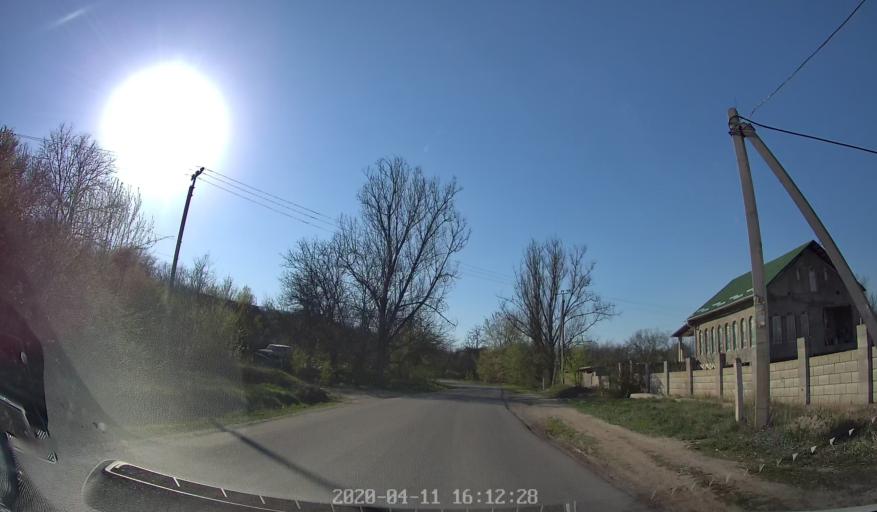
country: MD
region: Chisinau
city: Vadul lui Voda
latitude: 47.0697
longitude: 29.1213
